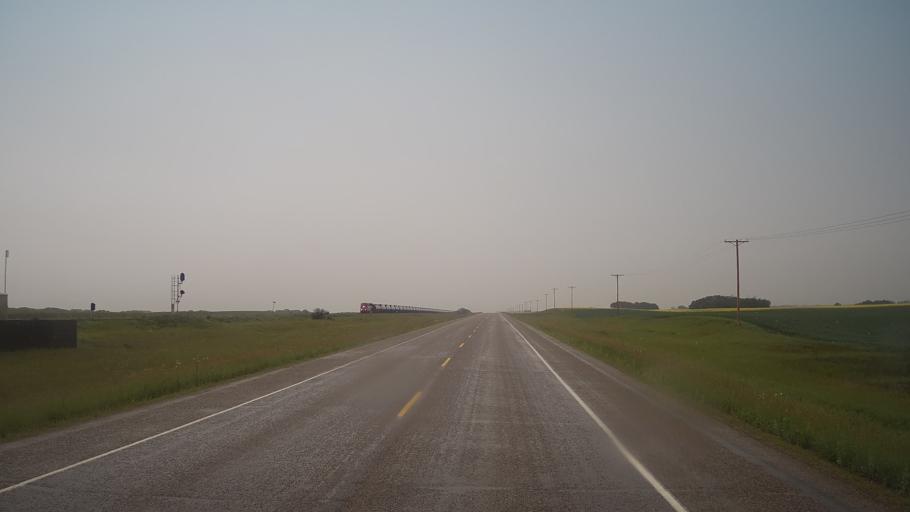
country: CA
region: Saskatchewan
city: Biggar
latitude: 52.1567
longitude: -108.2601
